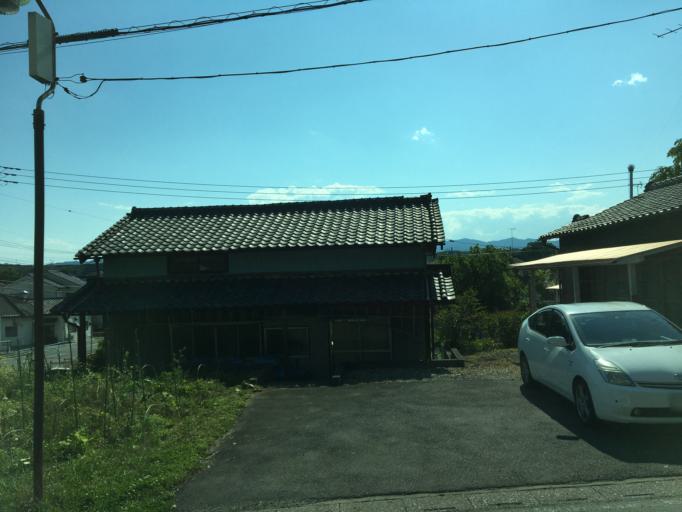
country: JP
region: Saitama
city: Morohongo
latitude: 35.9713
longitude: 139.3401
